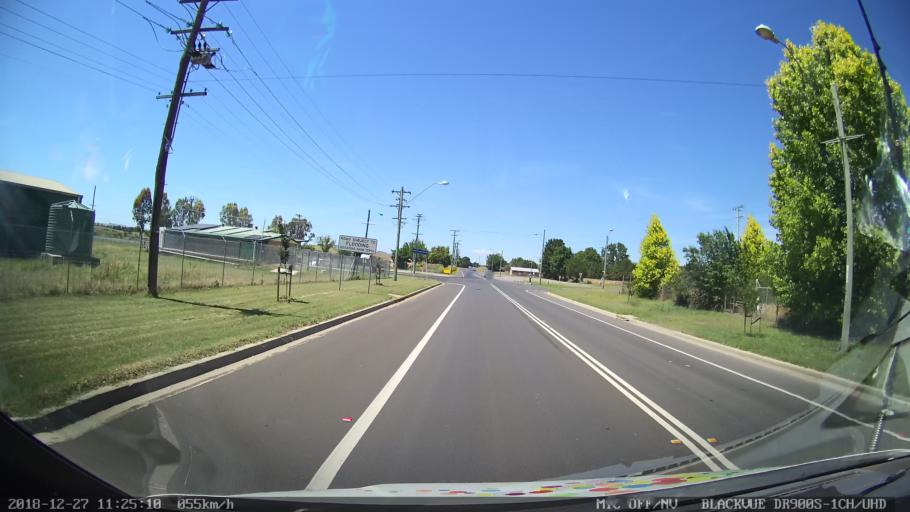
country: AU
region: New South Wales
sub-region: Bathurst Regional
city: Bathurst
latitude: -33.4394
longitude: 149.5786
